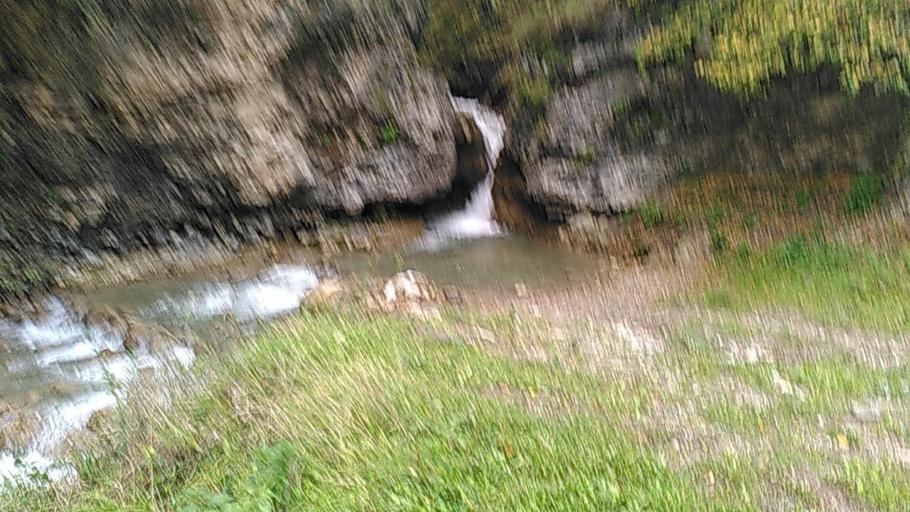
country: RU
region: Kabardino-Balkariya
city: Kamennomostskoye
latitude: 43.7198
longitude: 42.8439
